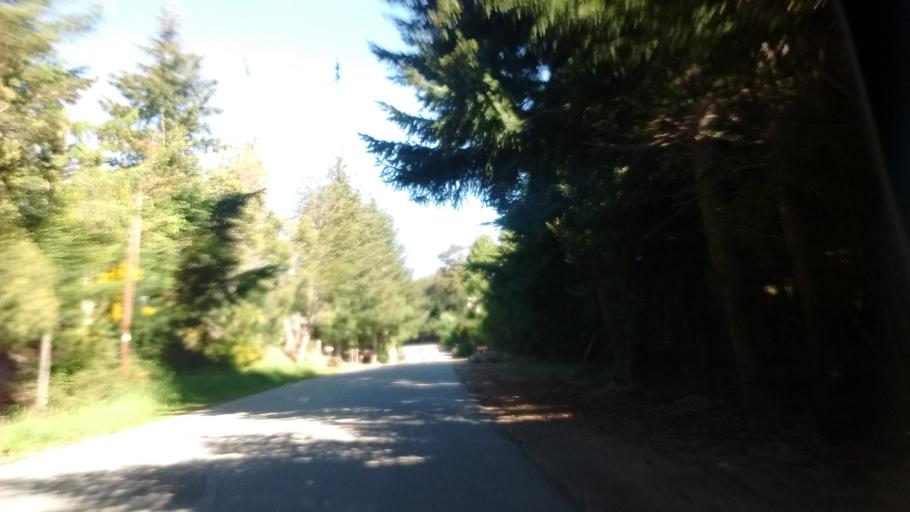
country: AR
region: Rio Negro
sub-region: Departamento de Bariloche
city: San Carlos de Bariloche
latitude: -41.0734
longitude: -71.5329
